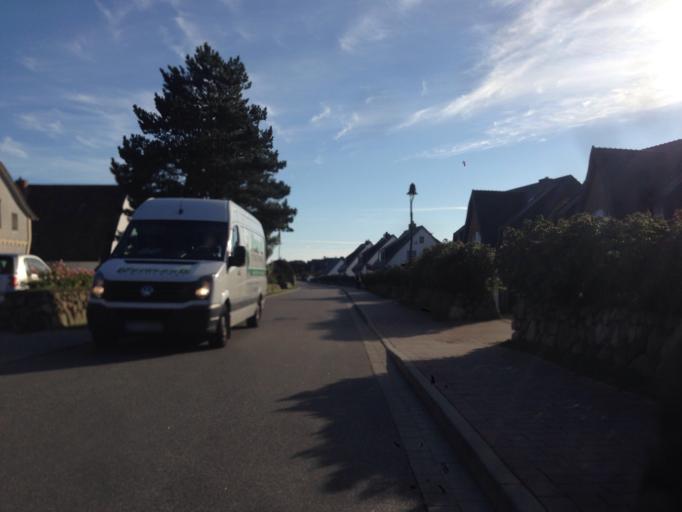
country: DE
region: Schleswig-Holstein
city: Tinnum
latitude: 54.9350
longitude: 8.3293
